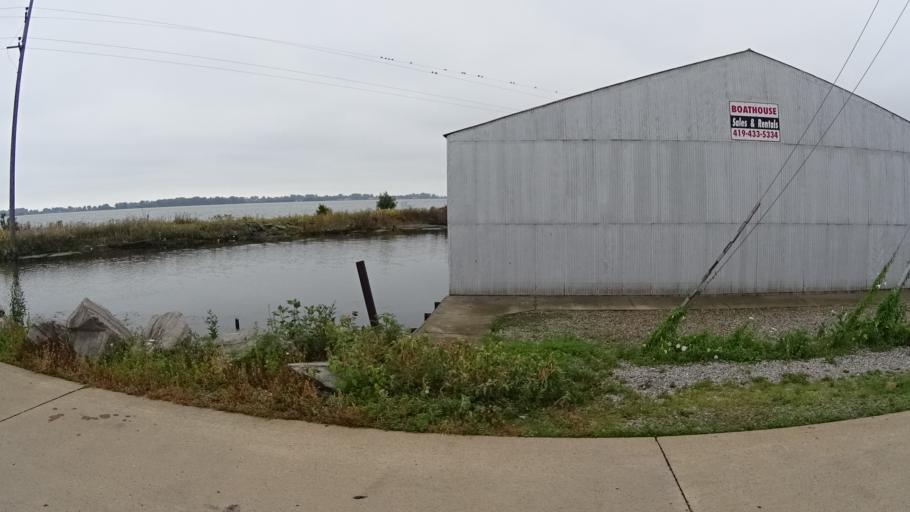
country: US
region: Ohio
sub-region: Erie County
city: Sandusky
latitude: 41.4566
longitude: -82.6961
